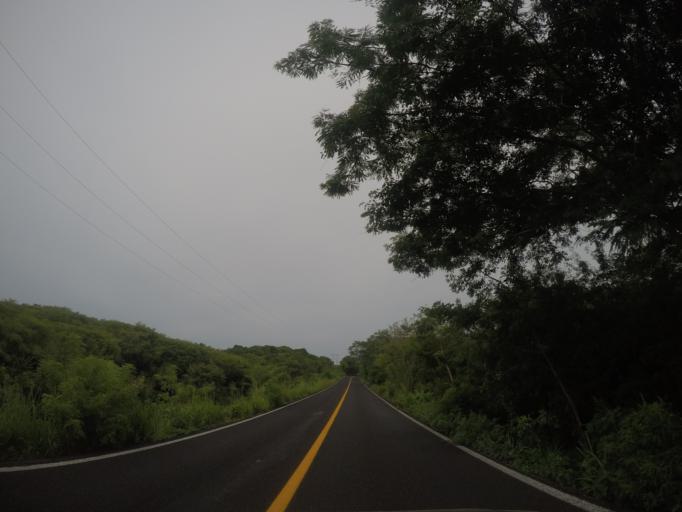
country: MX
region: Oaxaca
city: San Pedro Mixtepec
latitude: 15.9487
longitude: -97.2905
